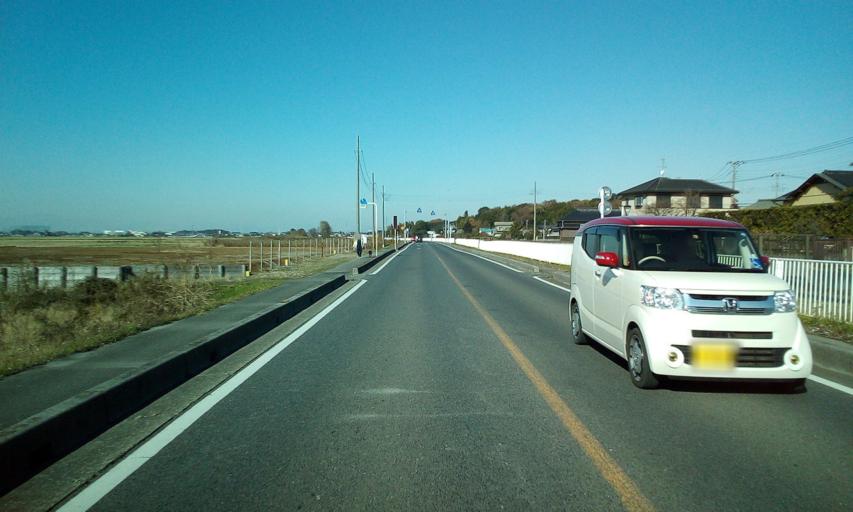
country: JP
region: Chiba
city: Noda
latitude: 35.9564
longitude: 139.8269
